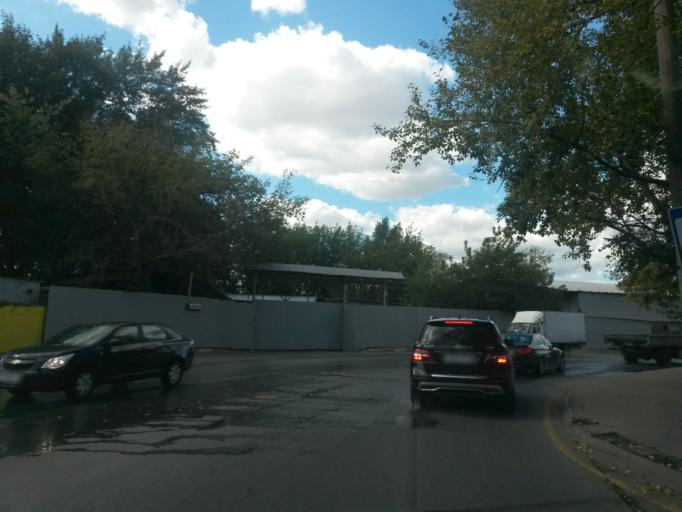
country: RU
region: Moskovskaya
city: Kozhukhovo
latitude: 55.7038
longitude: 37.7030
